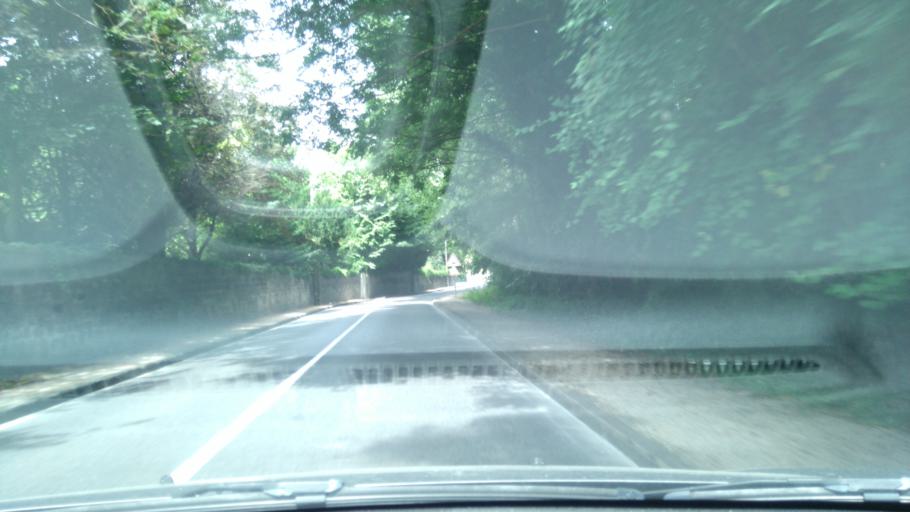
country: FR
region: Picardie
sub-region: Departement de l'Oise
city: Gouvieux
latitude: 49.1955
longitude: 2.4181
